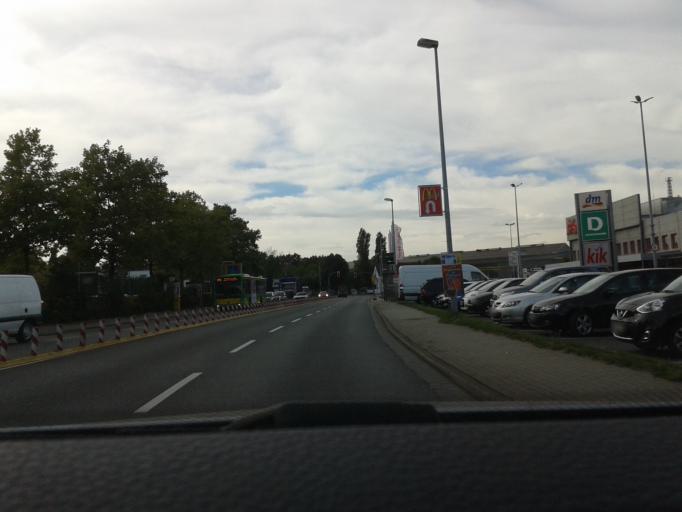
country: DE
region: North Rhine-Westphalia
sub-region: Regierungsbezirk Dusseldorf
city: Oberhausen
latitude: 51.4576
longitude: 6.8820
